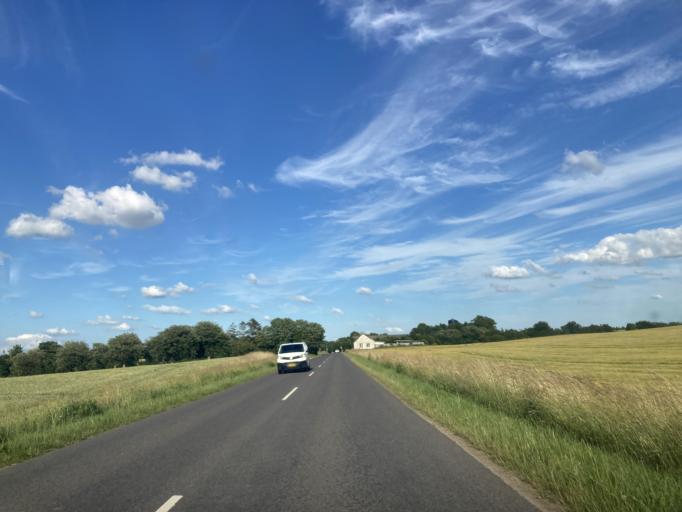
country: DK
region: South Denmark
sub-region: Kolding Kommune
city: Lunderskov
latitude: 55.4860
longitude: 9.3447
